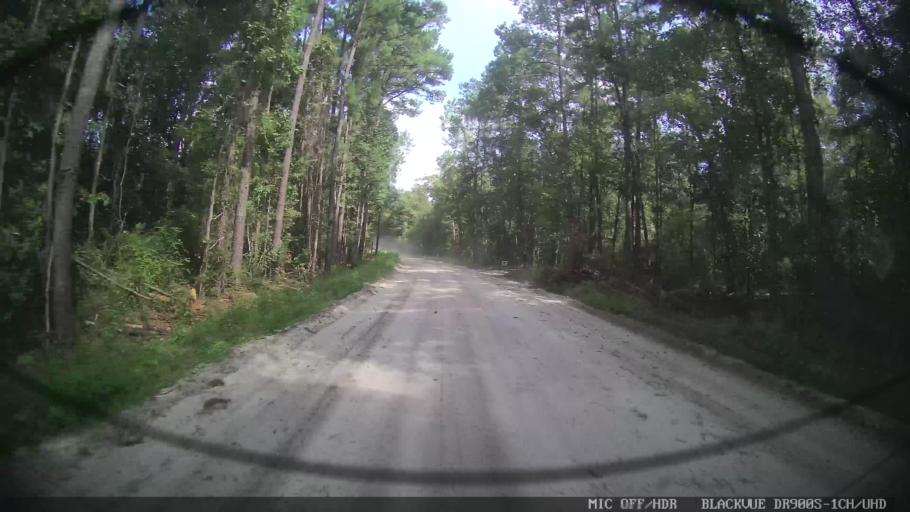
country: US
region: Florida
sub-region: Hamilton County
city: Jasper
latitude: 30.5518
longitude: -83.0889
